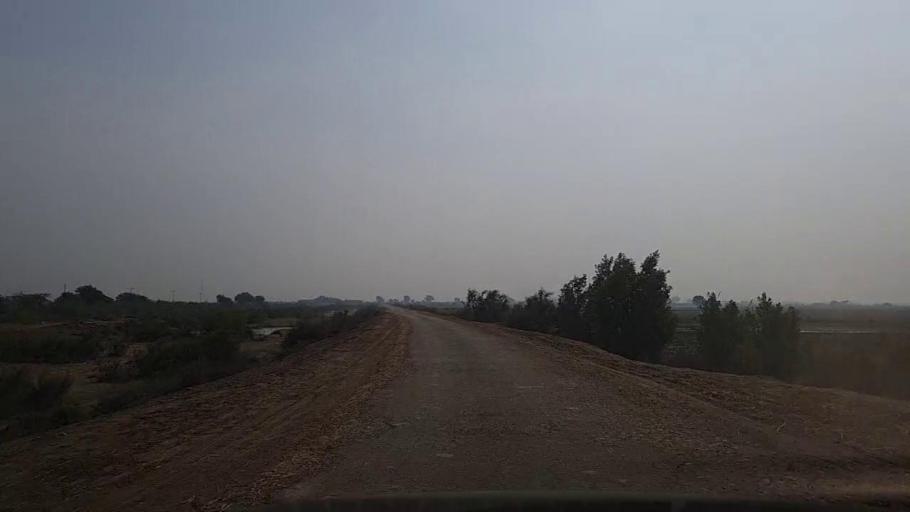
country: PK
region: Sindh
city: Mirpur Sakro
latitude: 24.3829
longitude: 67.7533
